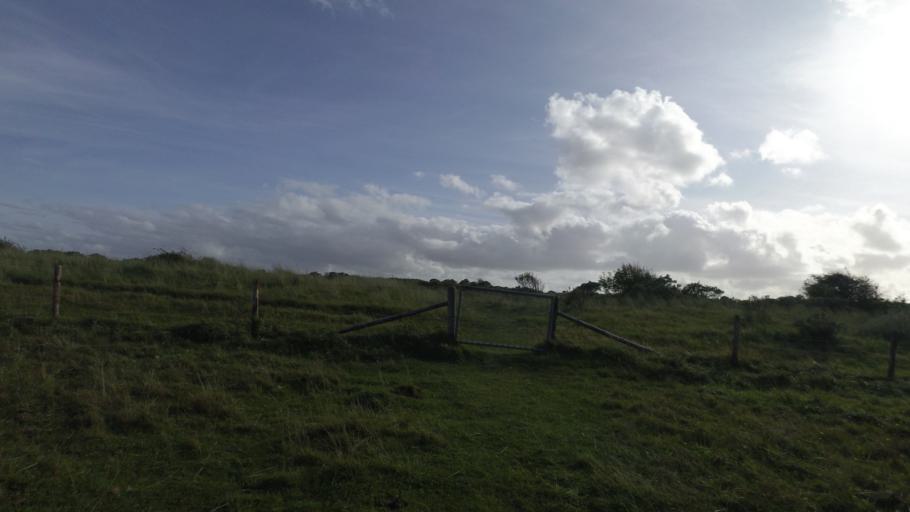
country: NL
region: Friesland
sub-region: Gemeente Ameland
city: Nes
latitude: 53.4579
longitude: 5.8358
